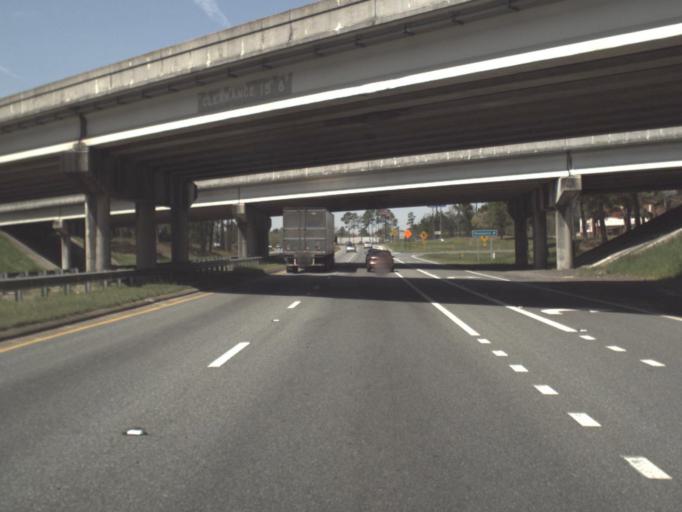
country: US
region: Florida
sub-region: Gadsden County
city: Midway
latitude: 30.4893
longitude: -84.4252
